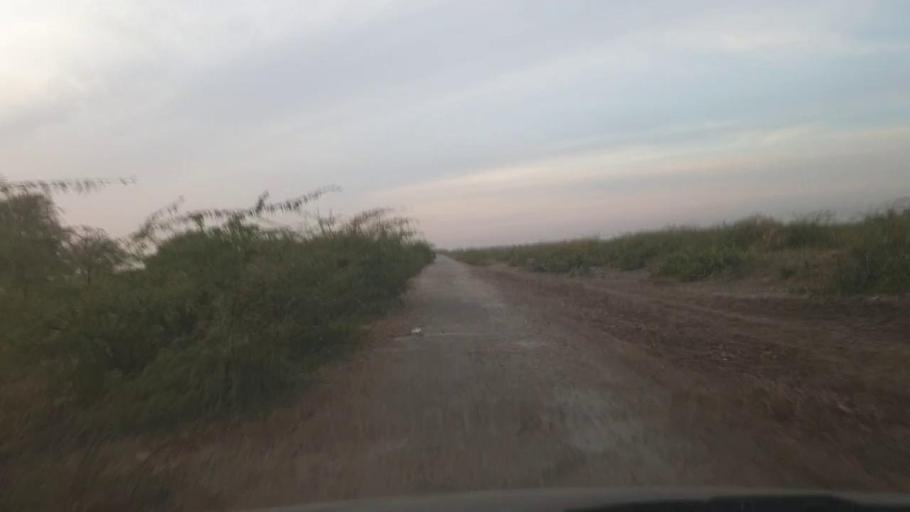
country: PK
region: Sindh
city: Kunri
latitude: 25.2293
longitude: 69.5333
